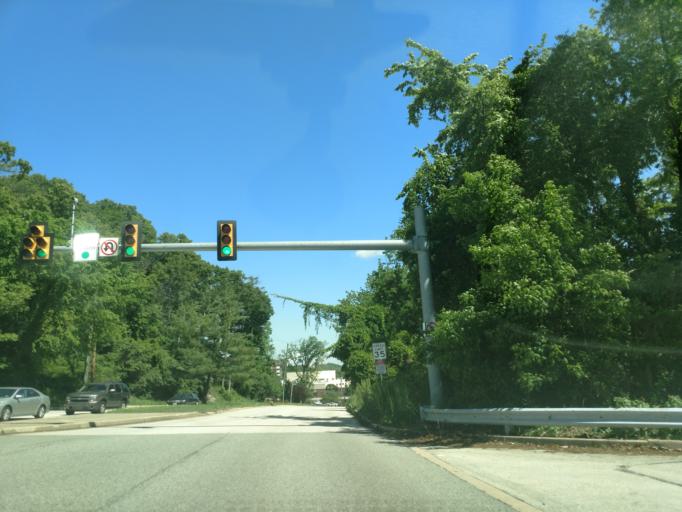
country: US
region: Pennsylvania
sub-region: Montgomery County
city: King of Prussia
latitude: 40.1031
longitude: -75.4007
